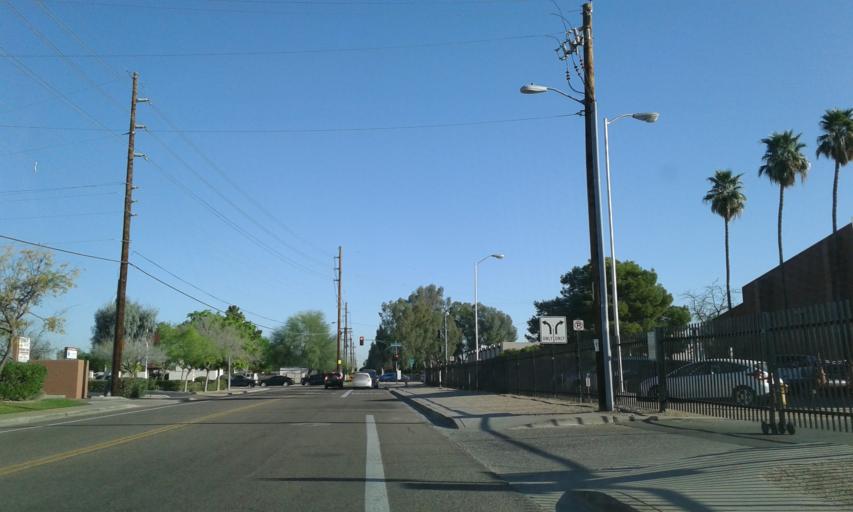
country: US
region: Arizona
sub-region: Maricopa County
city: Glendale
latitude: 33.5377
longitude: -112.1082
